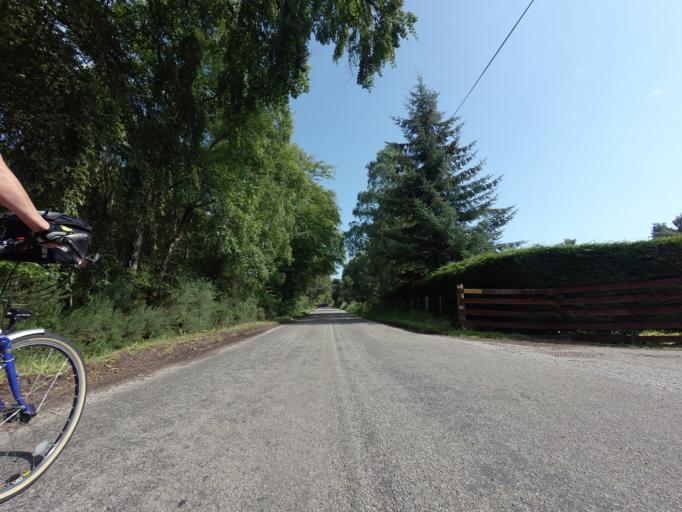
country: GB
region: Scotland
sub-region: Highland
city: Invergordon
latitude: 57.7307
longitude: -4.1924
